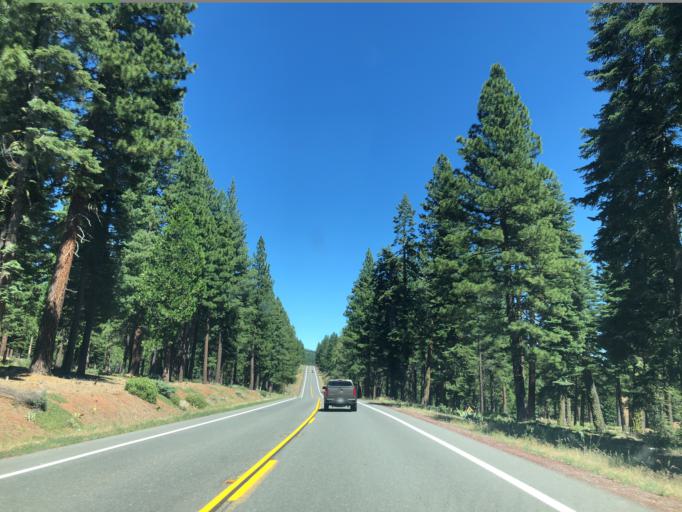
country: US
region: California
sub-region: Lassen County
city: Susanville
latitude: 40.4395
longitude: -120.8523
